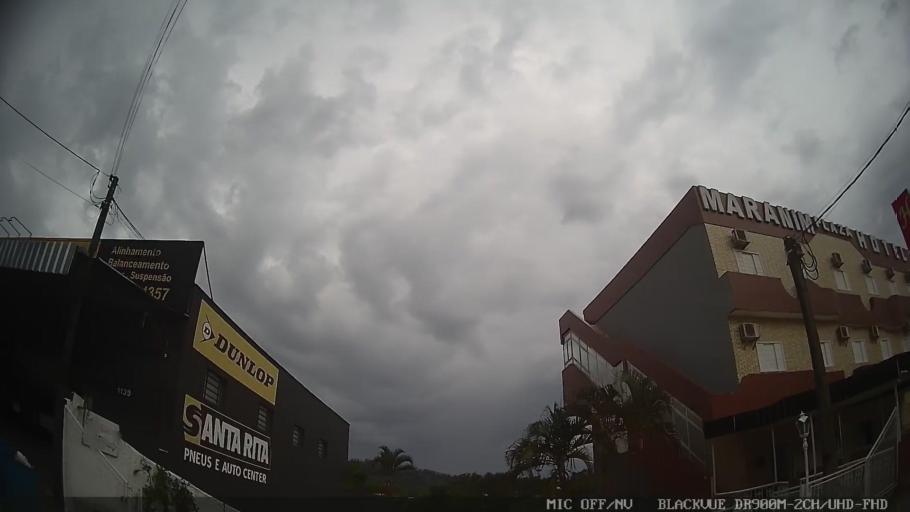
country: BR
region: Sao Paulo
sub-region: Amparo
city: Amparo
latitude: -22.6971
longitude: -46.7650
